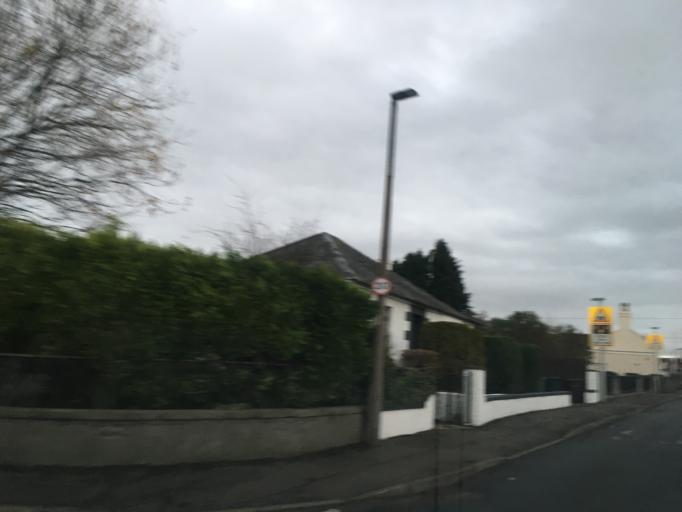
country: GB
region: Scotland
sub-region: Edinburgh
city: Colinton
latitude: 55.9196
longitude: -3.2652
